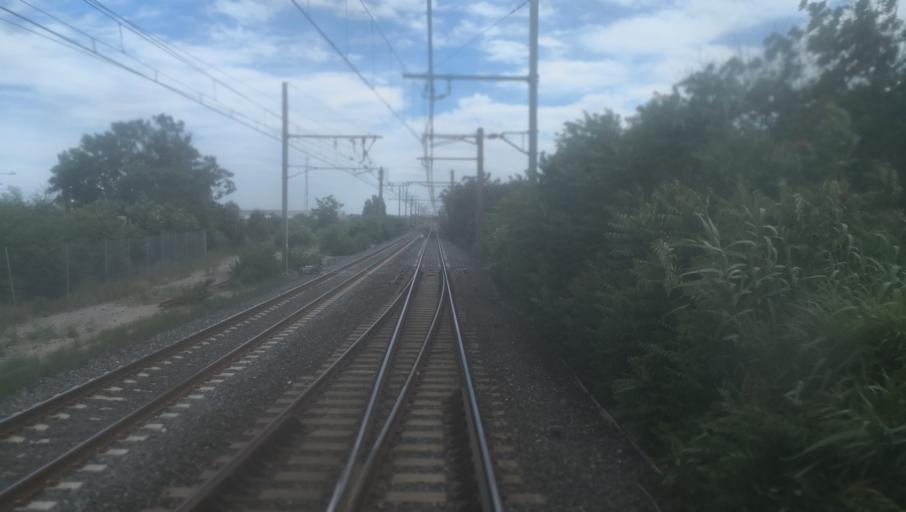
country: FR
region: Languedoc-Roussillon
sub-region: Departement de l'Herault
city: Frontignan
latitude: 43.4424
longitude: 3.7584
